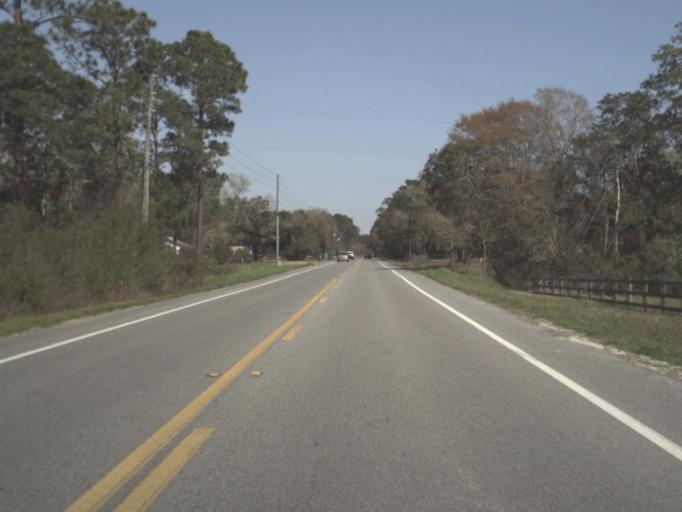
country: US
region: Florida
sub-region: Wakulla County
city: Crawfordville
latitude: 30.0758
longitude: -84.4290
